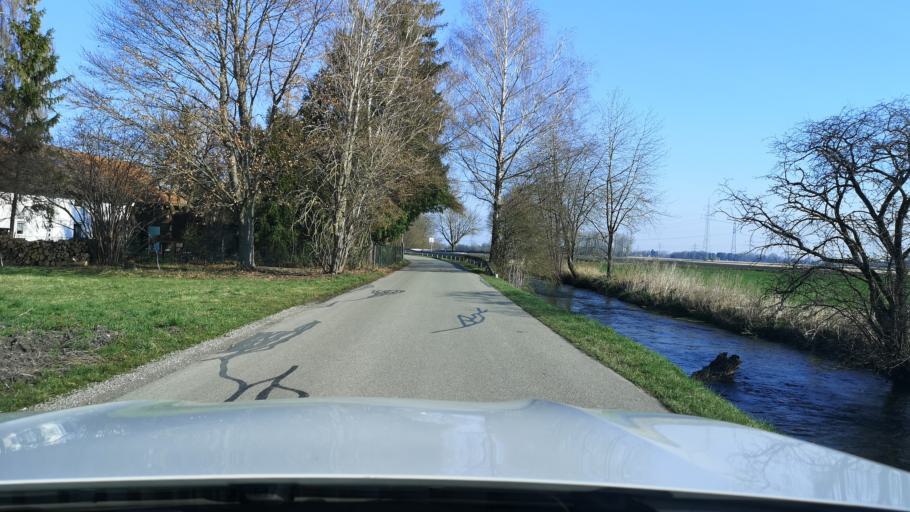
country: DE
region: Bavaria
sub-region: Upper Bavaria
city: Finsing
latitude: 48.2274
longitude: 11.8004
